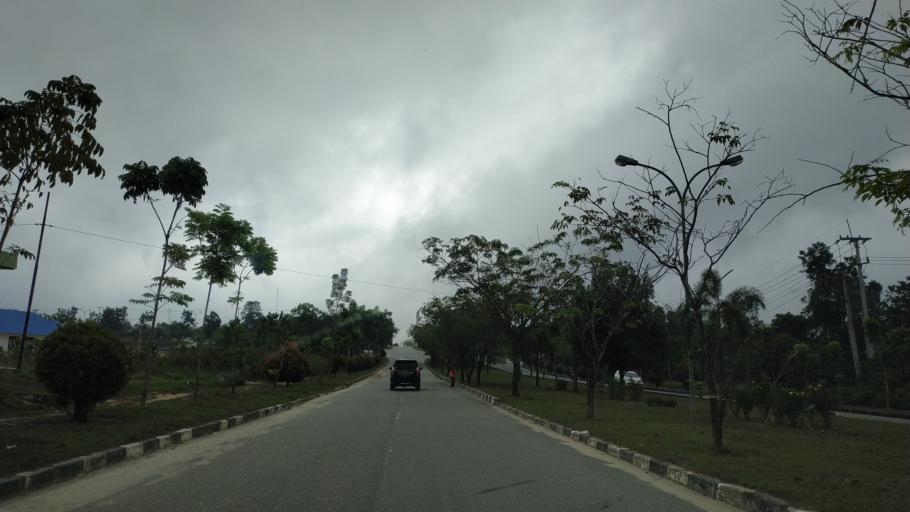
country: ID
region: Riau
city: Pangkalanbunut
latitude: 0.3873
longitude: 101.8245
